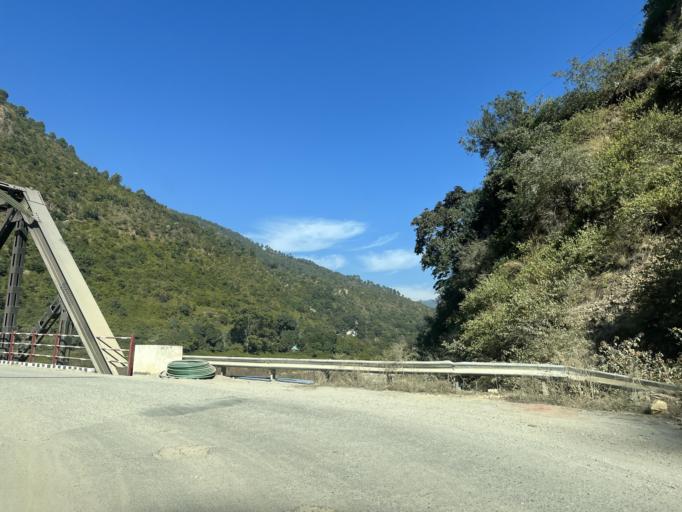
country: IN
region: Uttarakhand
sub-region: Naini Tal
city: Naini Tal
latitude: 29.5148
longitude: 79.4792
